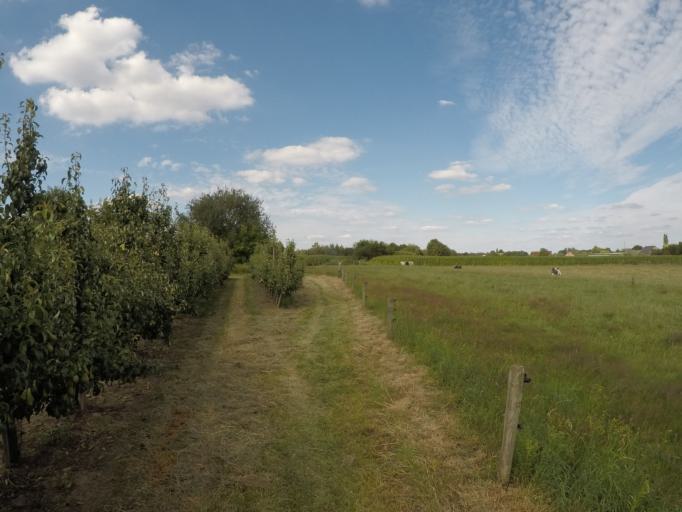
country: BE
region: Flanders
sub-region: Provincie Antwerpen
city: Ranst
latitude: 51.1693
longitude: 4.6070
